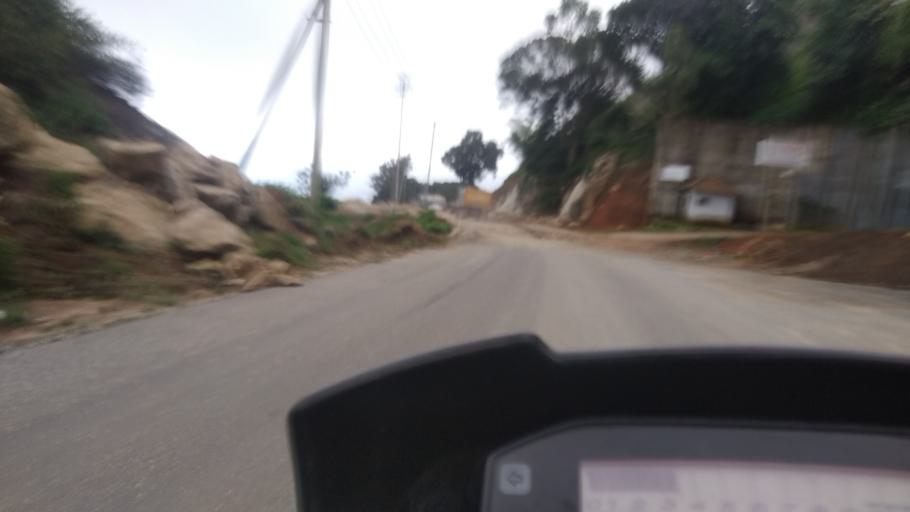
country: IN
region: Kerala
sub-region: Idukki
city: Munnar
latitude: 10.0320
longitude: 77.1607
